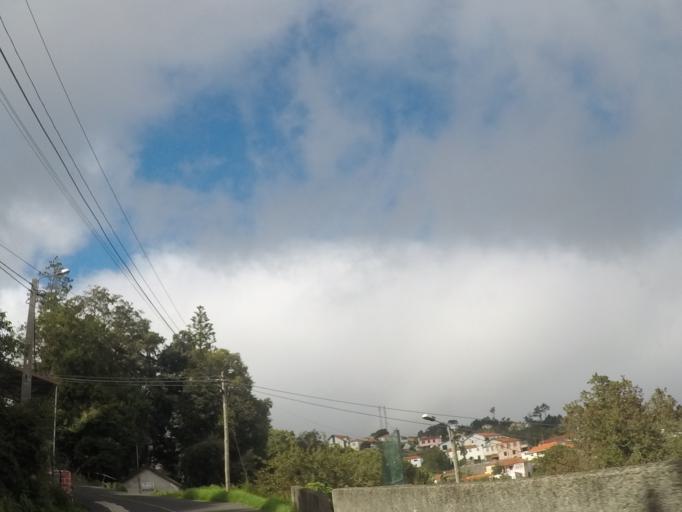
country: PT
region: Madeira
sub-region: Santa Cruz
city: Camacha
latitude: 32.6783
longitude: -16.8524
